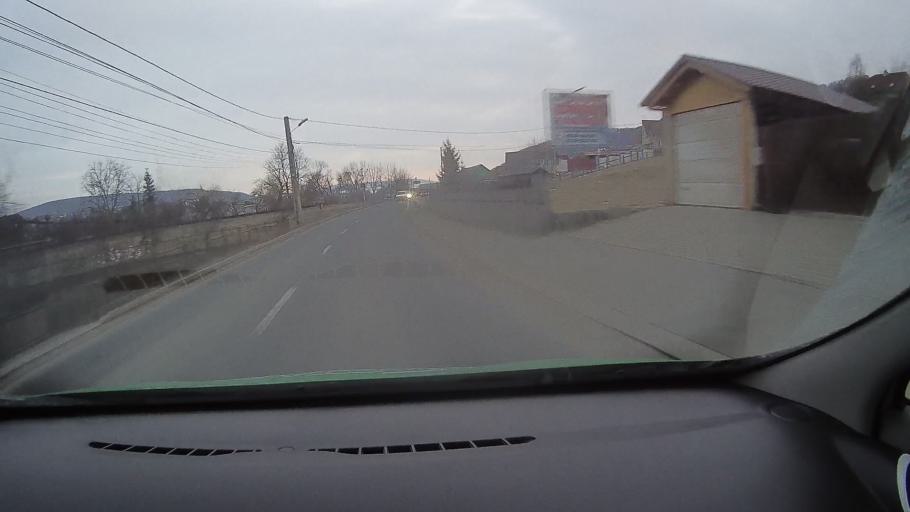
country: RO
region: Harghita
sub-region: Municipiul Odorheiu Secuiesc
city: Odorheiu Secuiesc
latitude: 46.3068
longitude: 25.2856
